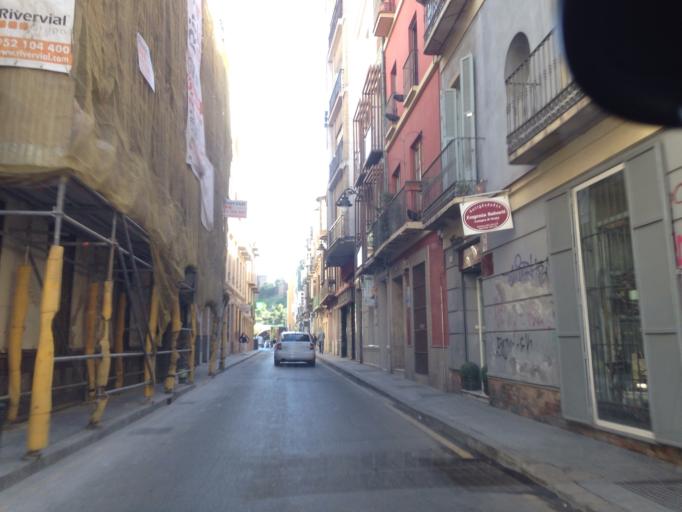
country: ES
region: Andalusia
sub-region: Provincia de Malaga
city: Malaga
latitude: 36.7236
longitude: -4.4192
